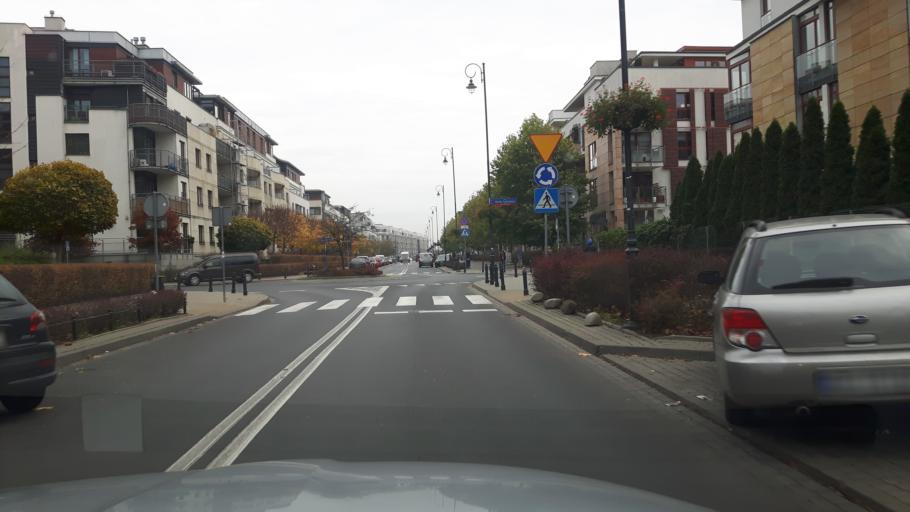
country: PL
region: Masovian Voivodeship
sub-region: Warszawa
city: Wilanow
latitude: 52.1607
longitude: 21.0782
